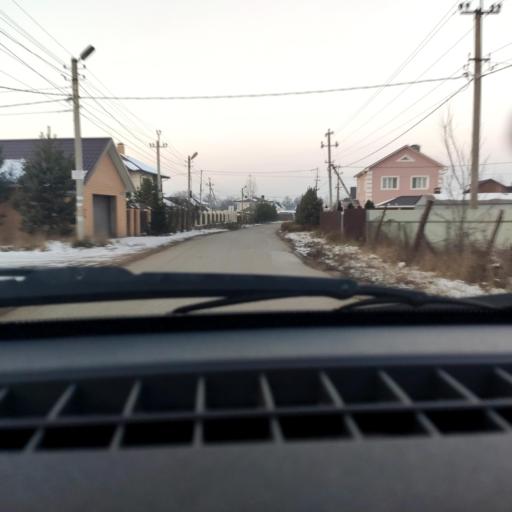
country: RU
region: Bashkortostan
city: Mikhaylovka
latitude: 54.7992
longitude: 55.9371
